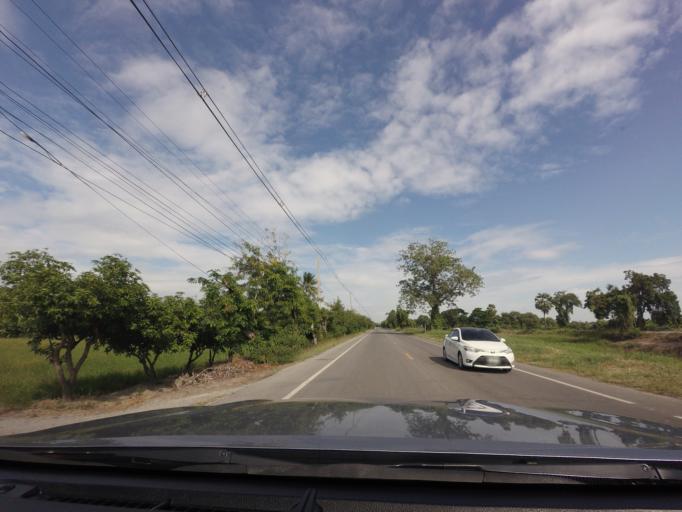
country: TH
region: Suphan Buri
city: Suphan Buri
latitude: 14.5354
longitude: 100.1119
